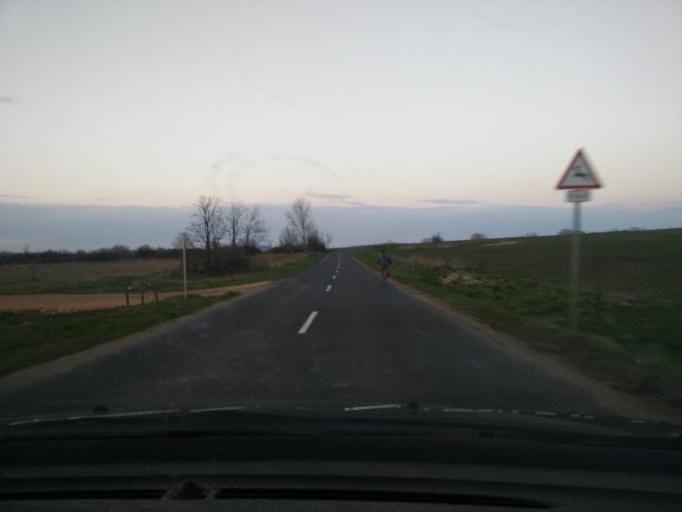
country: HU
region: Veszprem
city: Csabrendek
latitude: 47.0458
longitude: 17.3297
